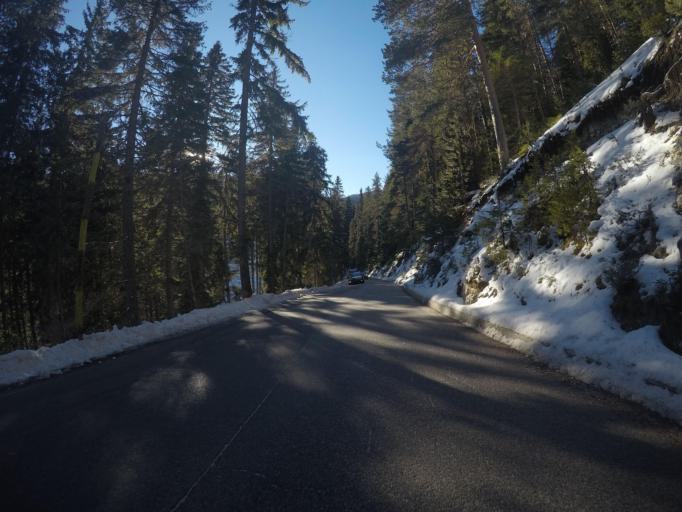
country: BG
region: Blagoevgrad
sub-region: Obshtina Bansko
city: Bansko
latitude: 41.7851
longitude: 23.4529
